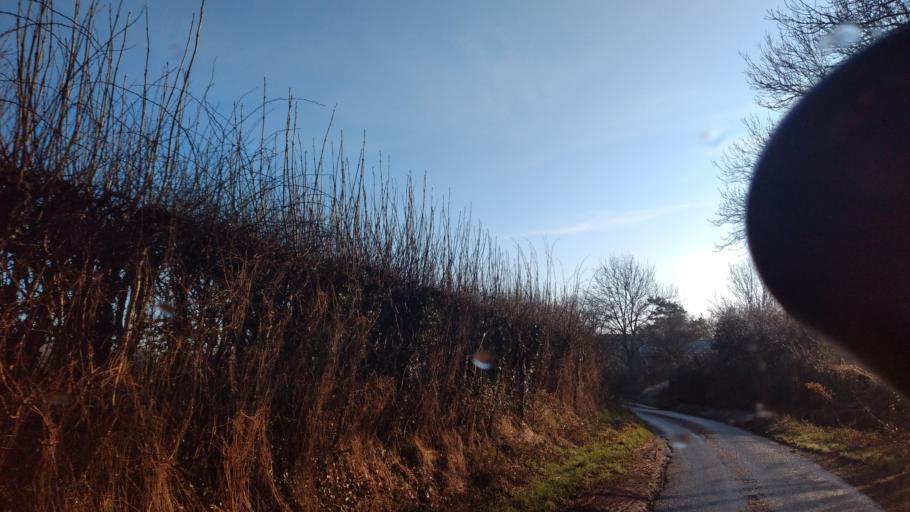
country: GB
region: England
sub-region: Wiltshire
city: Lacock
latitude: 51.4293
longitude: -2.1345
